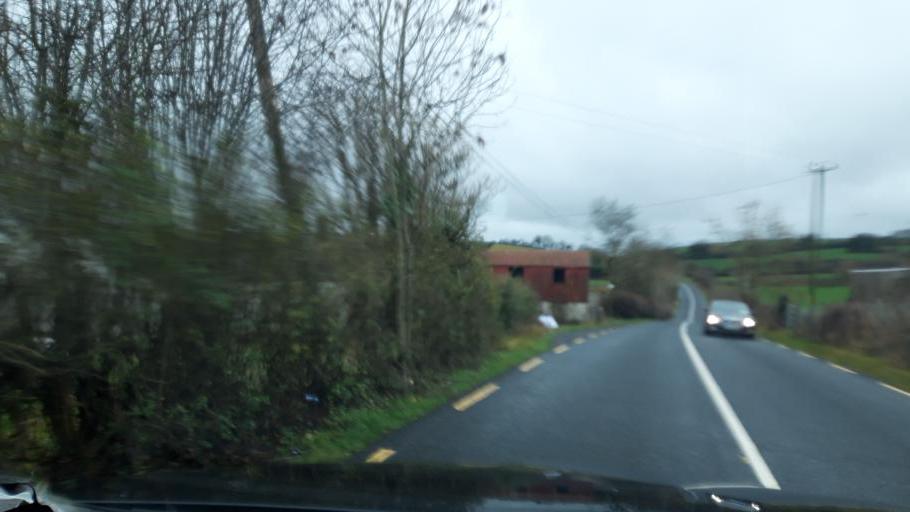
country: IE
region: Ulster
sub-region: County Monaghan
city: Castleblayney
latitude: 54.0775
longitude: -6.6811
